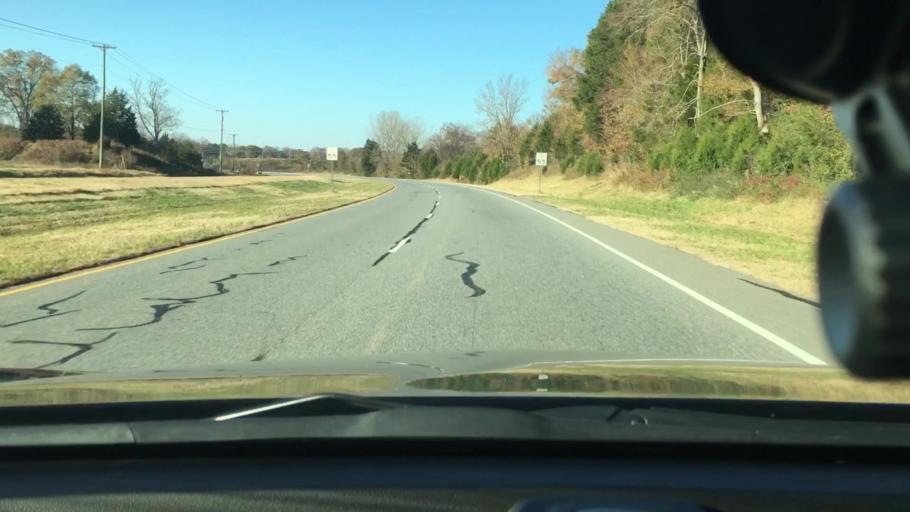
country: US
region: North Carolina
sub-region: Cabarrus County
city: Concord
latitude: 35.3850
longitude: -80.5219
